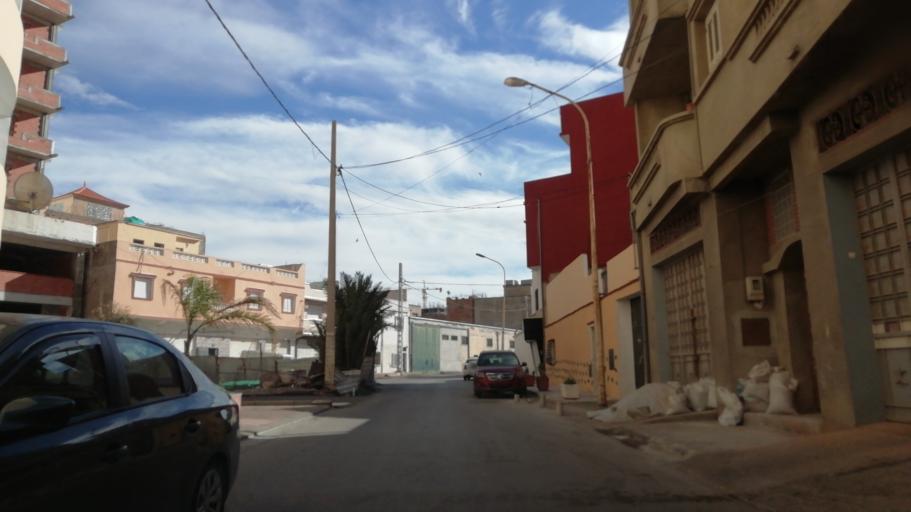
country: DZ
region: Oran
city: Oran
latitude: 35.7024
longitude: -0.6206
